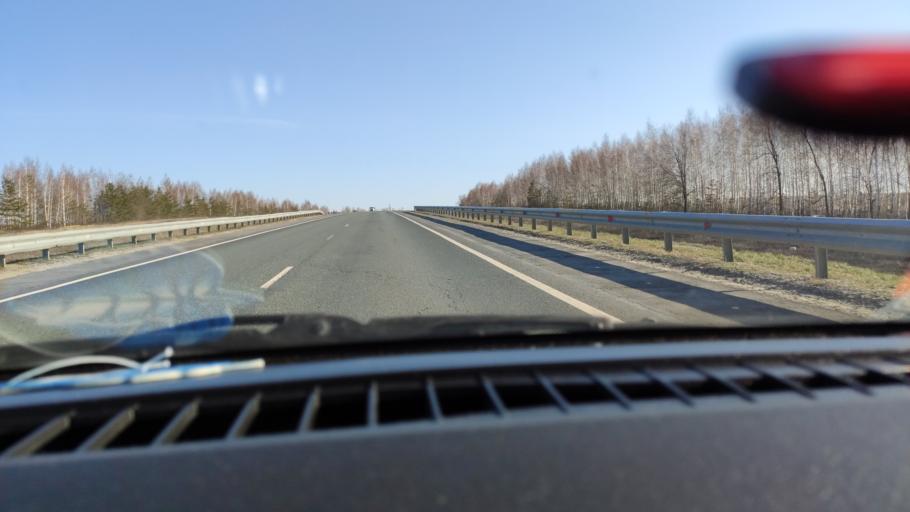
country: RU
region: Saratov
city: Dukhovnitskoye
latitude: 52.8330
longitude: 48.2403
